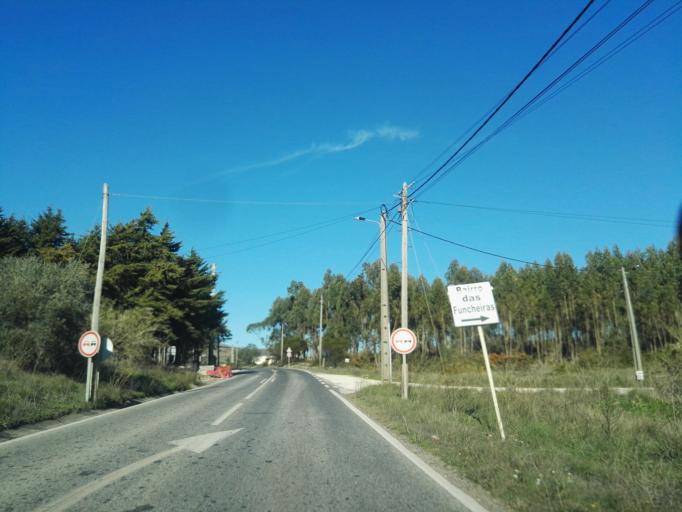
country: PT
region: Lisbon
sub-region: Mafra
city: Venda do Pinheiro
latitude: 38.8884
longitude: -9.1883
